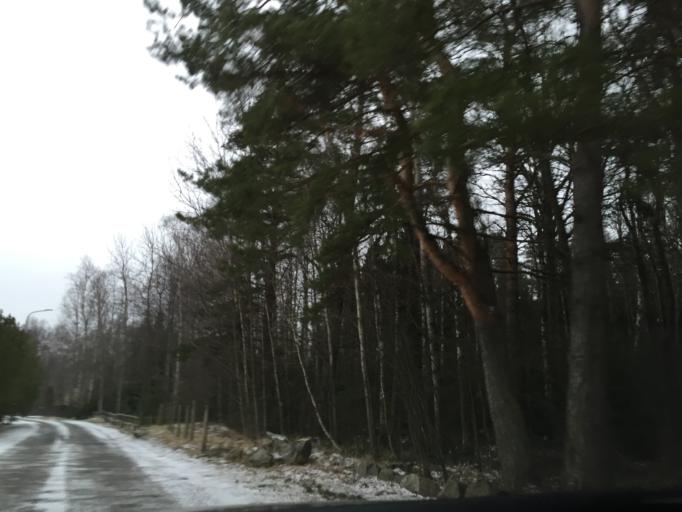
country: LV
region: Saulkrastu
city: Saulkrasti
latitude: 57.5000
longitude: 24.3833
